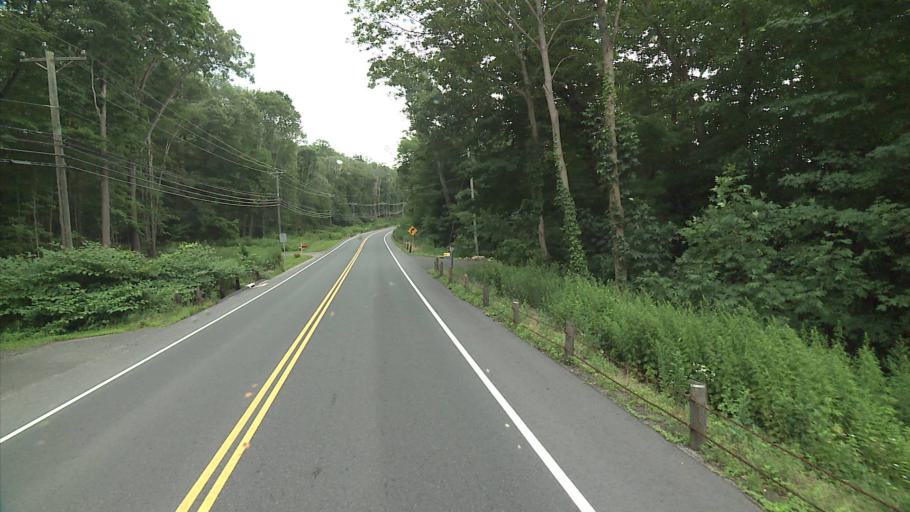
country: US
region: Connecticut
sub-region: New Haven County
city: Southbury
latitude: 41.4711
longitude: -73.1816
